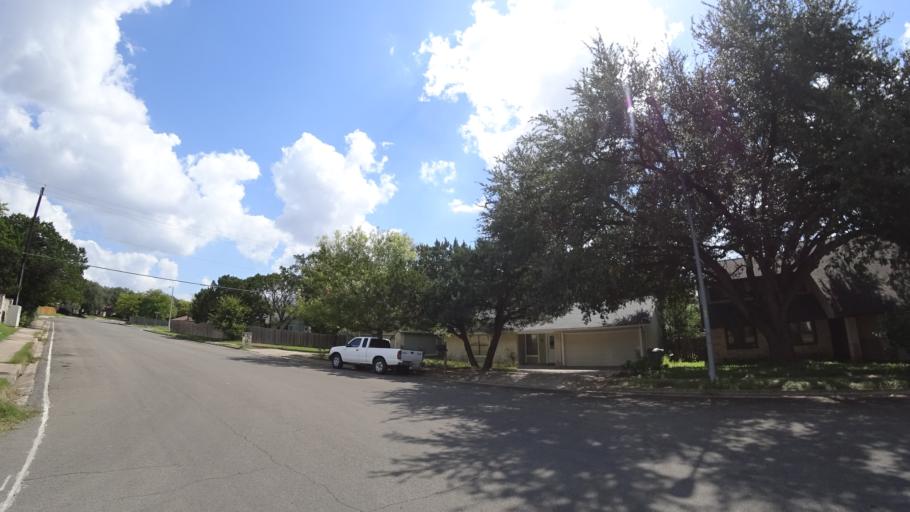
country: US
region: Texas
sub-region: Travis County
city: Onion Creek
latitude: 30.1895
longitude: -97.7886
